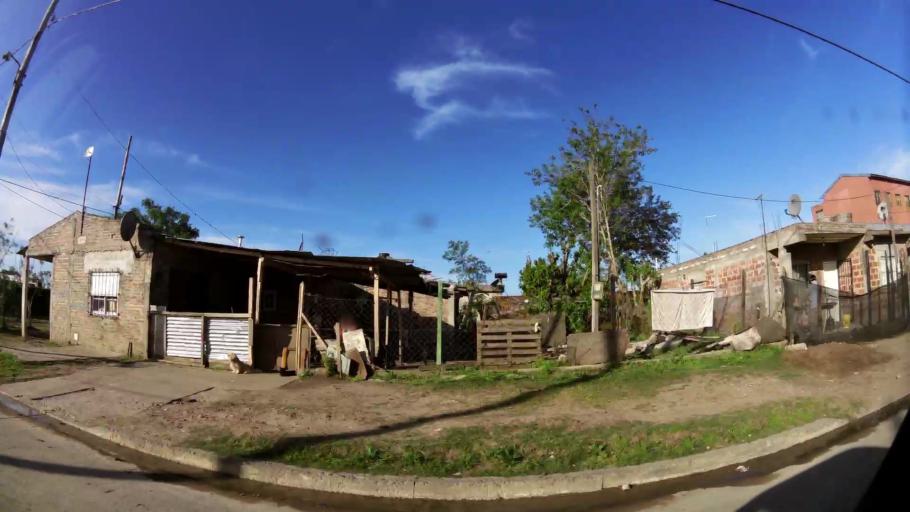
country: AR
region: Buenos Aires
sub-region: Partido de Quilmes
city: Quilmes
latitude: -34.8224
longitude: -58.2121
